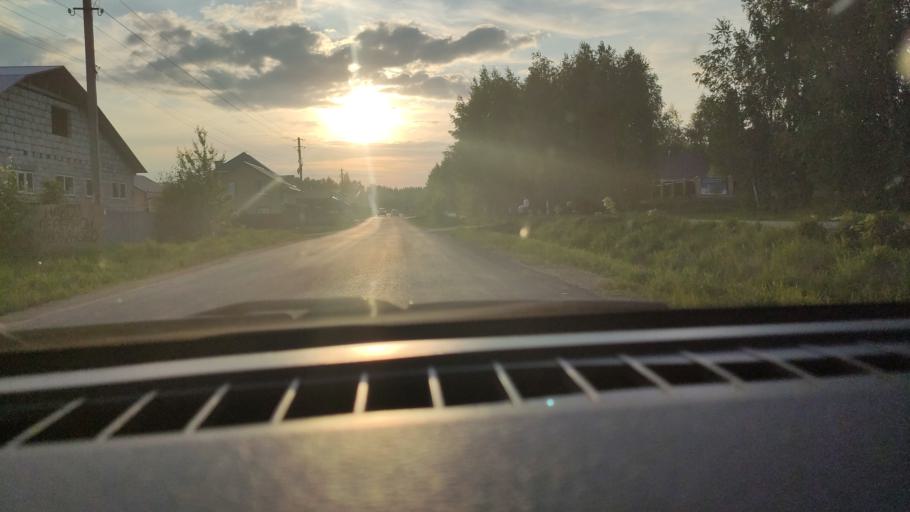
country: RU
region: Perm
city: Kondratovo
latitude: 58.0568
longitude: 56.0102
